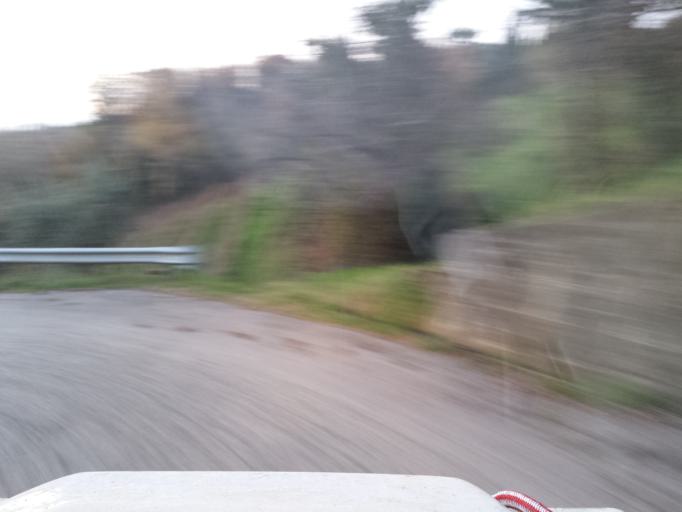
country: SI
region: Brda
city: Dobrovo
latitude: 45.9878
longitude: 13.4887
